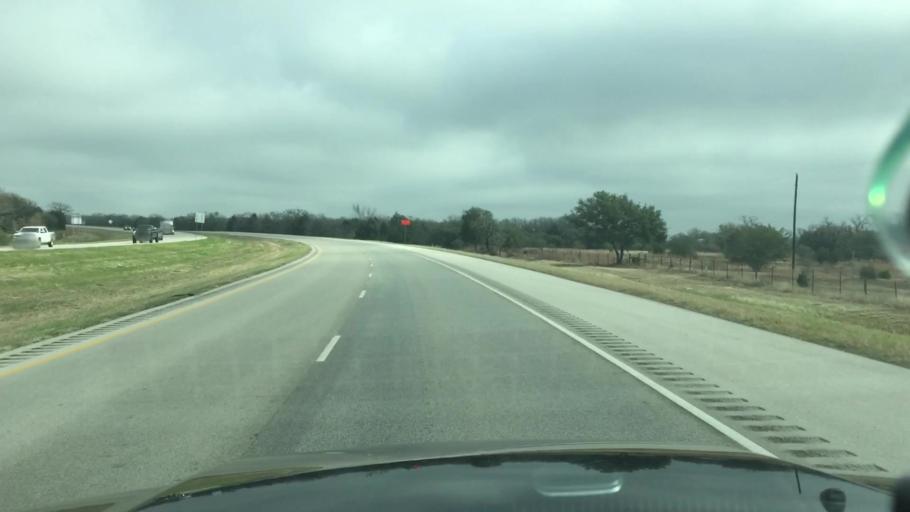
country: US
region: Texas
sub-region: Lee County
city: Giddings
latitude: 30.1408
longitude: -96.7663
